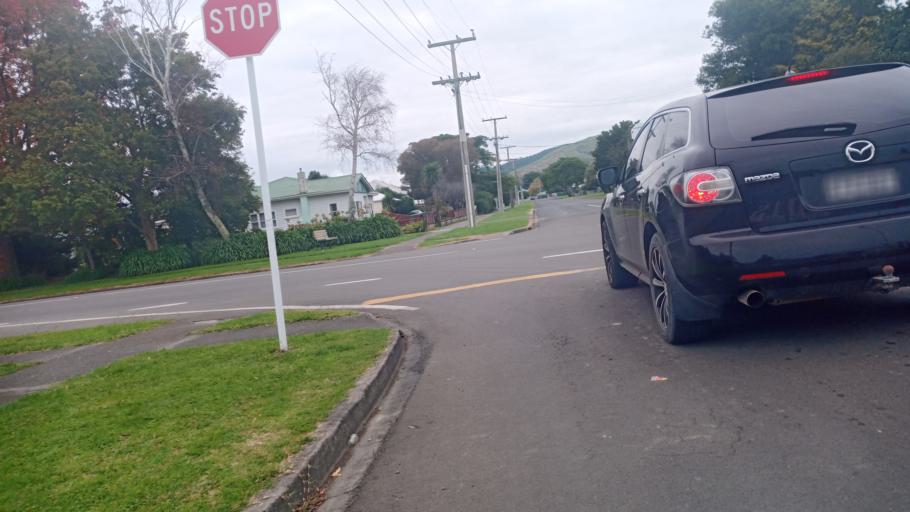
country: NZ
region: Gisborne
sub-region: Gisborne District
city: Gisborne
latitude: -38.6735
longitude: 178.0451
